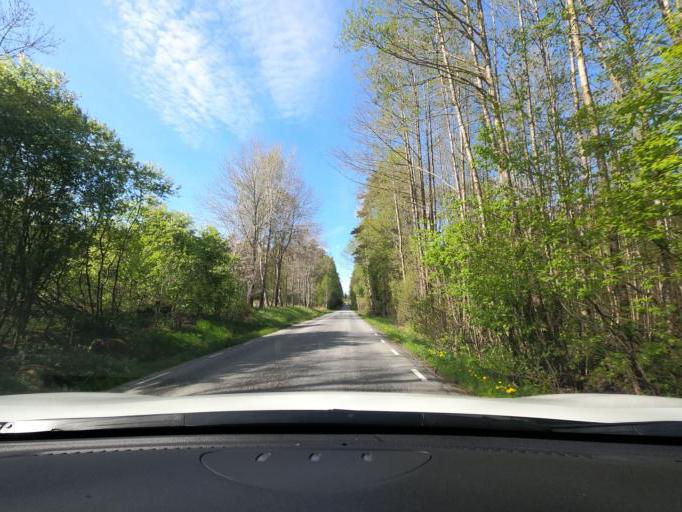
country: SE
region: Vaestra Goetaland
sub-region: Marks Kommun
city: Kinna
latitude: 57.4803
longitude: 12.5679
